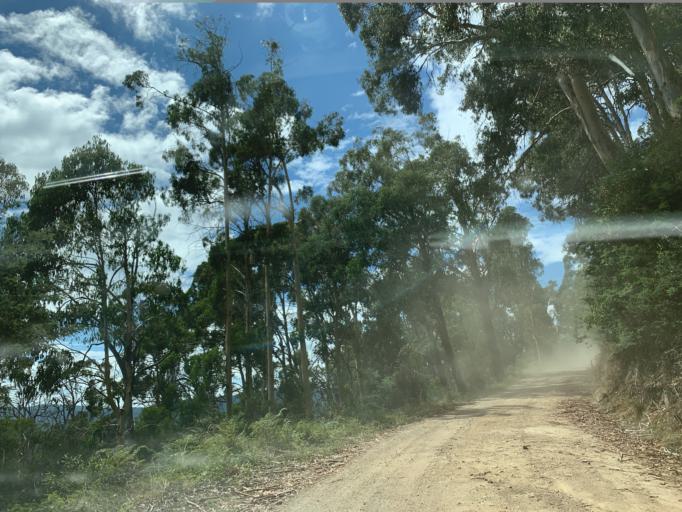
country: AU
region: Victoria
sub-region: Mansfield
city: Mansfield
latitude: -37.0998
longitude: 146.5045
